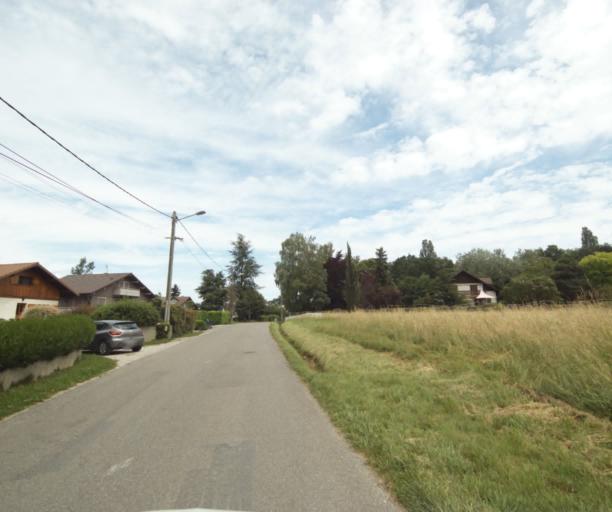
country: FR
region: Rhone-Alpes
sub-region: Departement de la Haute-Savoie
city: Anthy-sur-Leman
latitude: 46.3496
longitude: 6.4119
